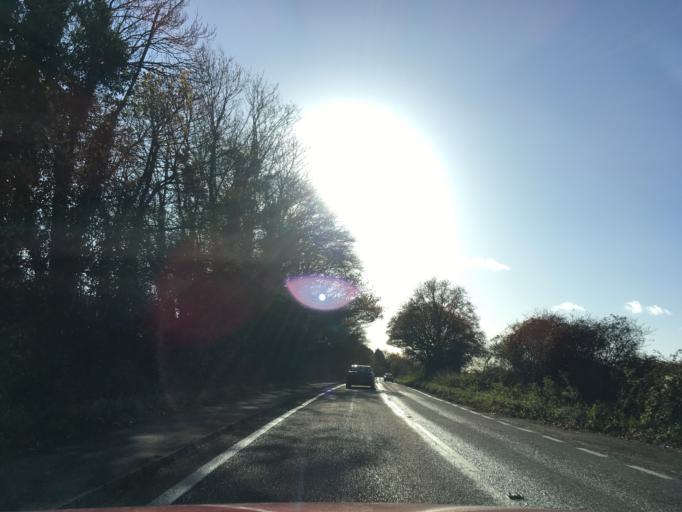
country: GB
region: England
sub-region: Hampshire
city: Colden Common
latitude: 51.0068
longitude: -1.3179
